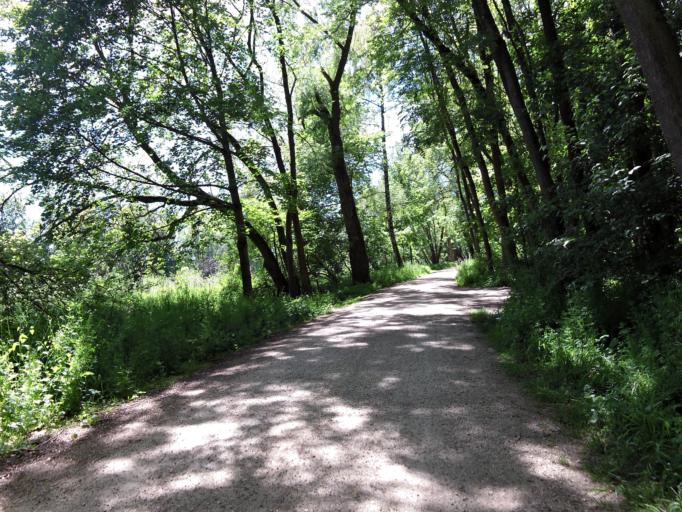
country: DE
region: Bavaria
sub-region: Upper Bavaria
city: Freising
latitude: 48.4016
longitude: 11.7597
